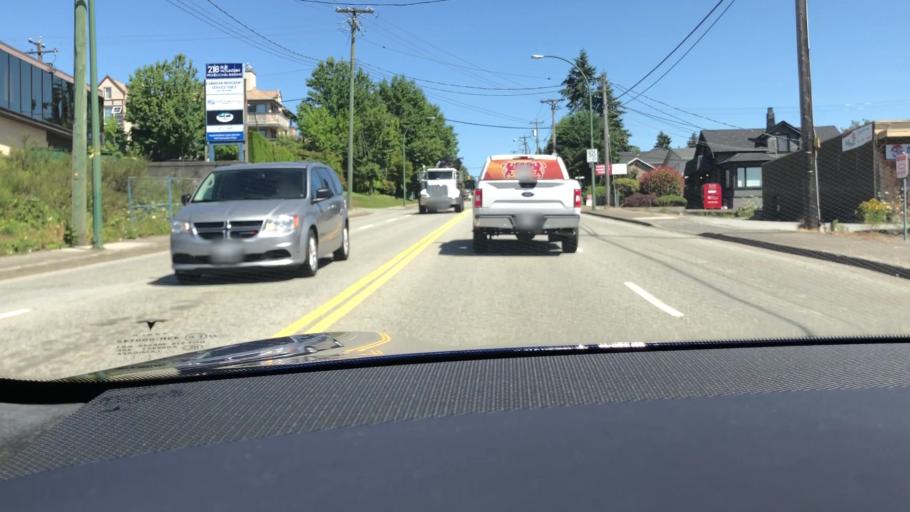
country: CA
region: British Columbia
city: New Westminster
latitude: 49.2372
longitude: -122.8731
